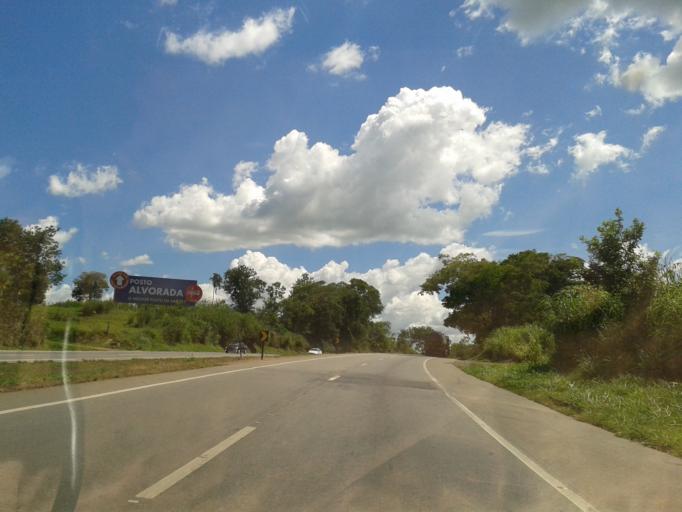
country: BR
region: Goias
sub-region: Piracanjuba
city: Piracanjuba
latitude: -17.2269
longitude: -49.2295
